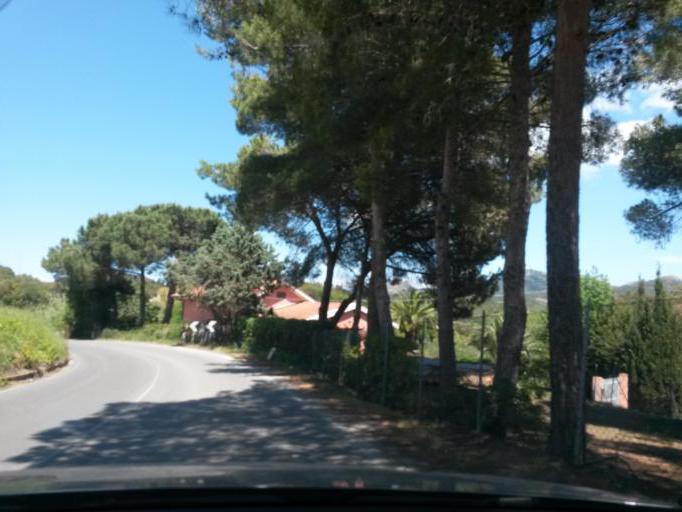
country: IT
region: Tuscany
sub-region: Provincia di Livorno
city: Capoliveri
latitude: 42.7717
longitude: 10.3453
